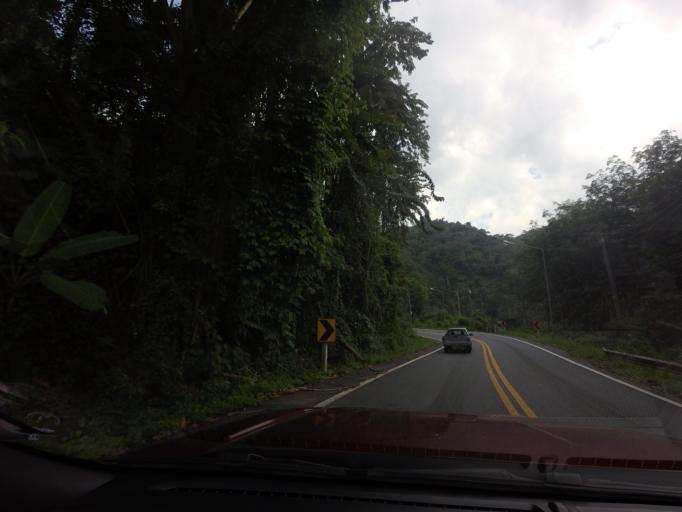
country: TH
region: Yala
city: Than To
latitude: 6.0371
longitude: 101.1993
